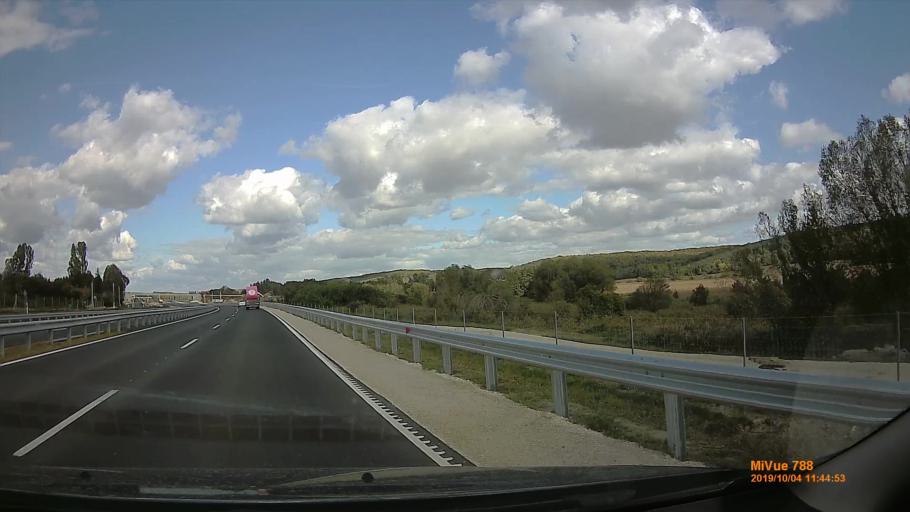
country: HU
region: Somogy
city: Karad
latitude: 46.6188
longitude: 17.7973
